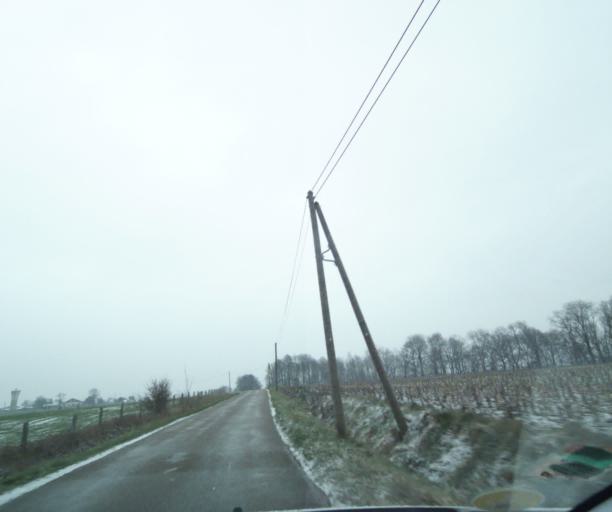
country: FR
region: Champagne-Ardenne
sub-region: Departement de la Haute-Marne
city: Wassy
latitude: 48.4662
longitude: 5.0352
